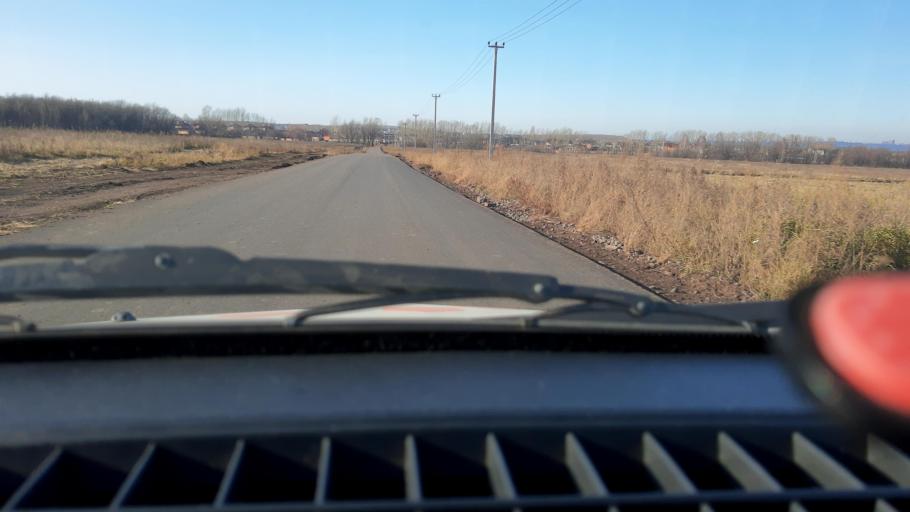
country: RU
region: Bashkortostan
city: Kabakovo
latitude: 54.6230
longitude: 56.1511
